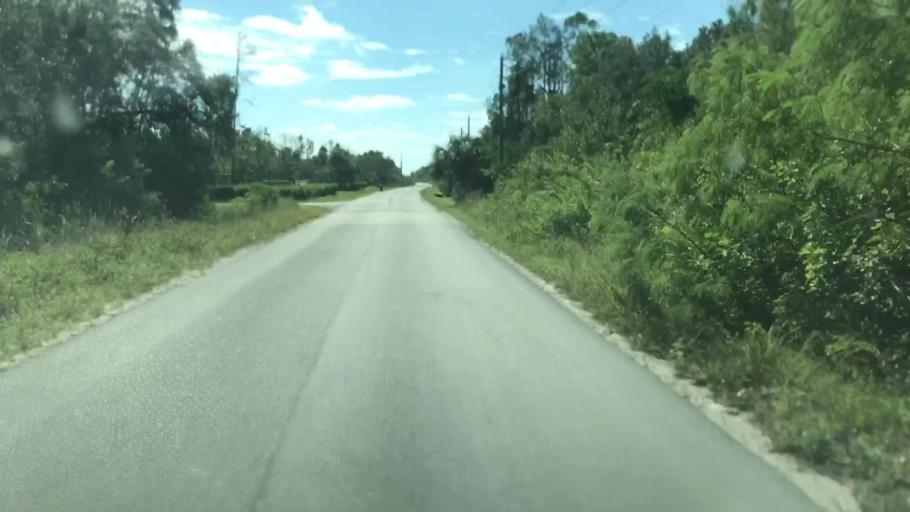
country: US
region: Florida
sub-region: Lee County
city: Bonita Springs
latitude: 26.3539
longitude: -81.7387
